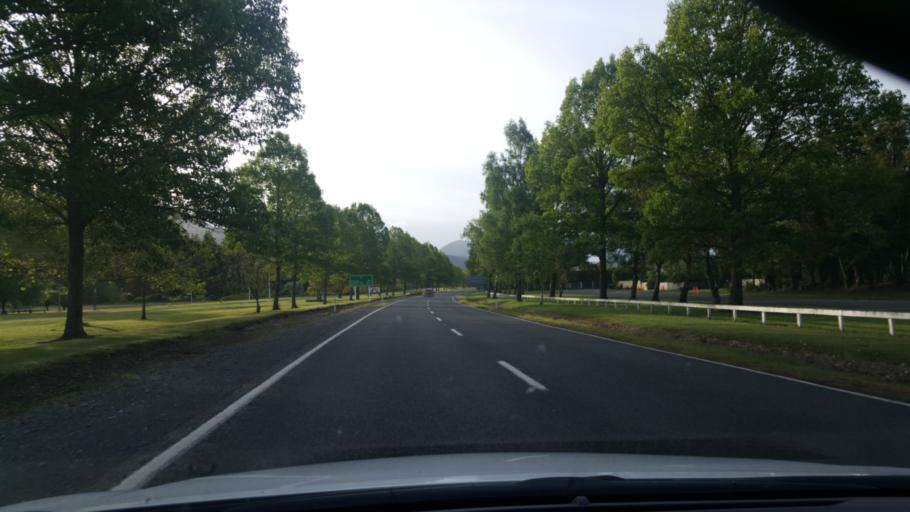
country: NZ
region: Waikato
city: Turangi
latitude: -38.9952
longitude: 175.8018
